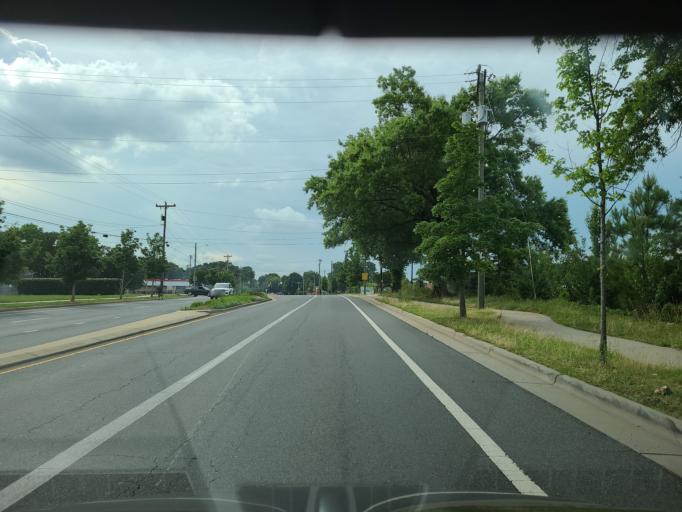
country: US
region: North Carolina
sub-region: Mecklenburg County
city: Charlotte
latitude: 35.2087
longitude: -80.7550
